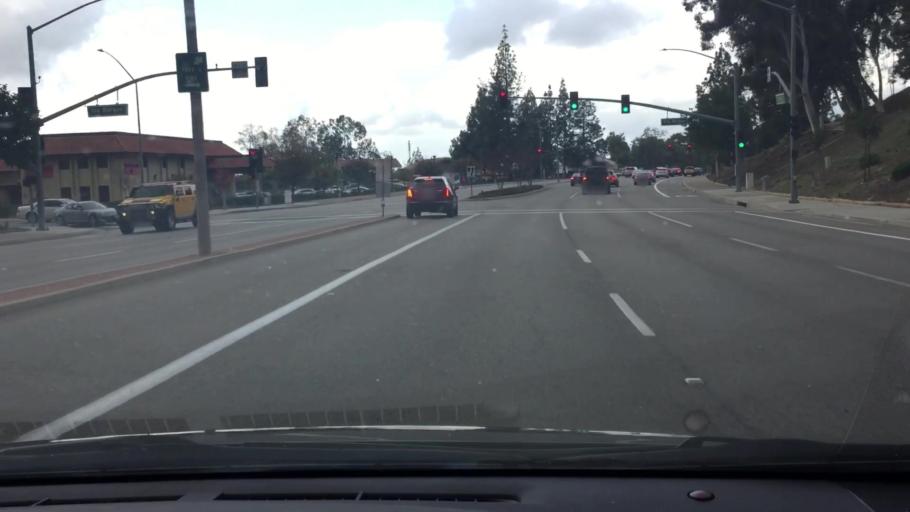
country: US
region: California
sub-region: Orange County
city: Mission Viejo
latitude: 33.6232
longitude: -117.6585
